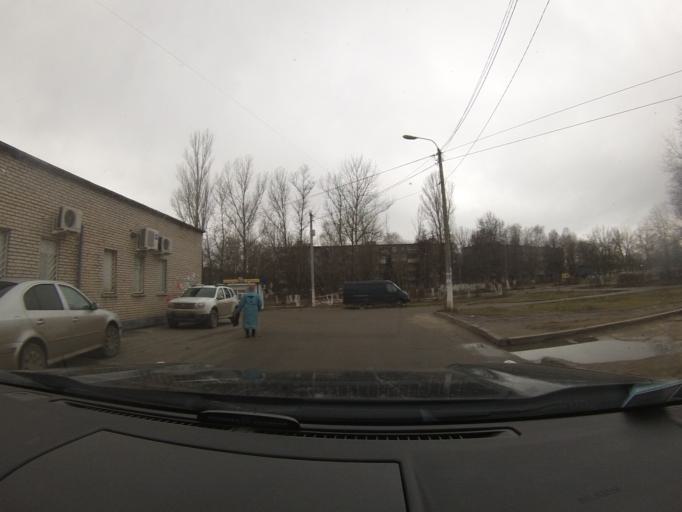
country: RU
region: Moskovskaya
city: Peski
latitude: 55.2753
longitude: 38.7491
